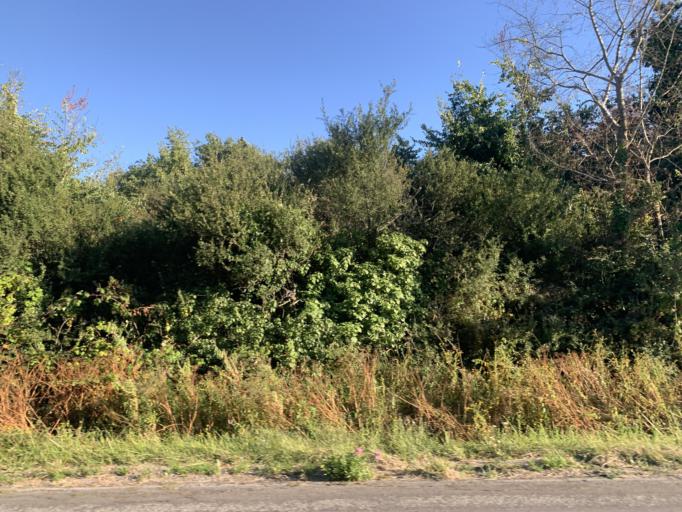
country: FR
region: Pays de la Loire
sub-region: Departement de la Loire-Atlantique
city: Pornichet
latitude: 47.2594
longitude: -2.2935
